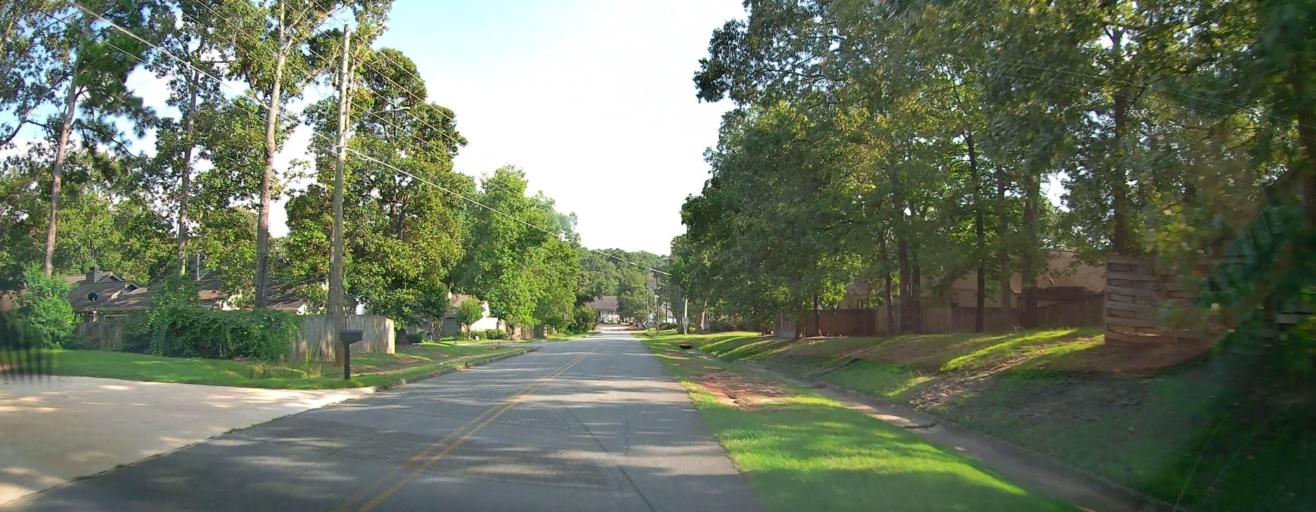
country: US
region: Georgia
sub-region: Houston County
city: Warner Robins
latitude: 32.5877
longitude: -83.6323
